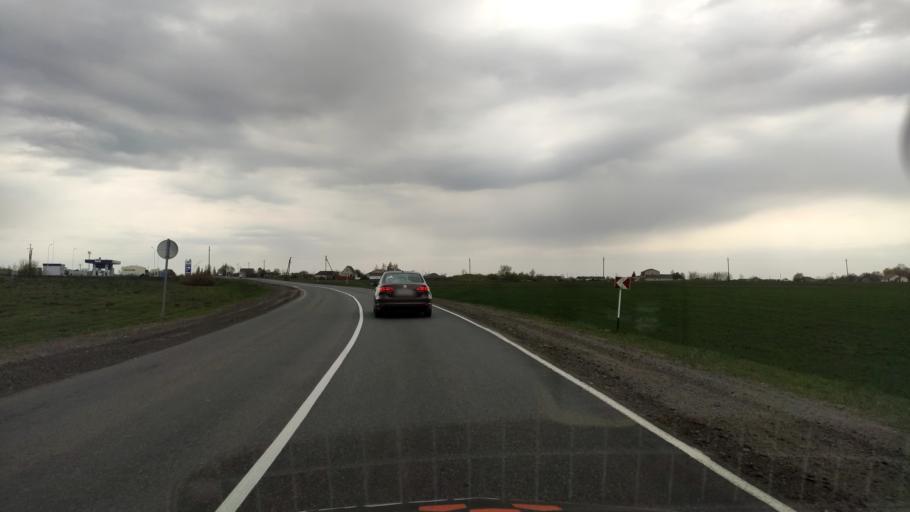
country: RU
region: Kursk
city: Gorshechnoye
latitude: 51.5375
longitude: 38.0226
